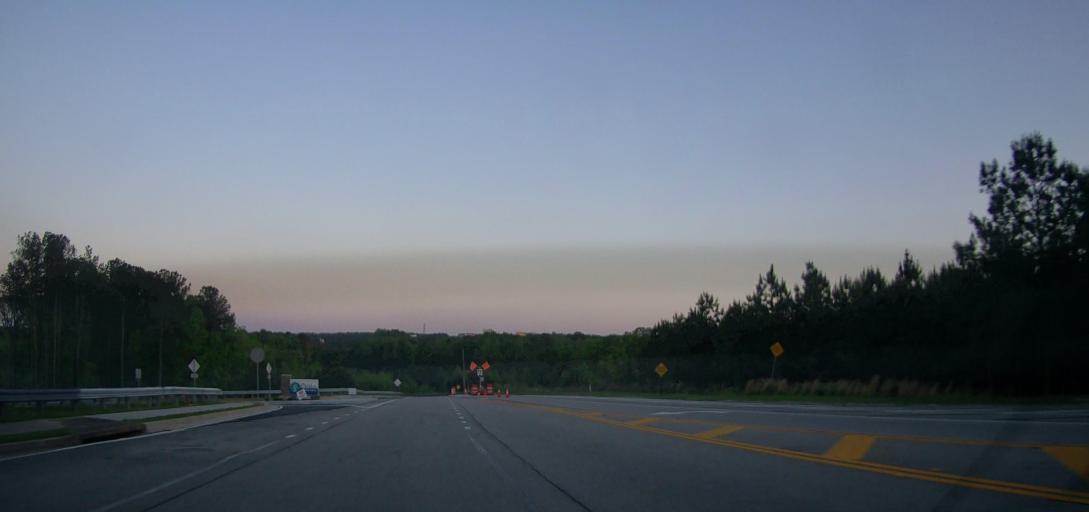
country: US
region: Georgia
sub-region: Henry County
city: Stockbridge
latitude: 33.5050
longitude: -84.2265
